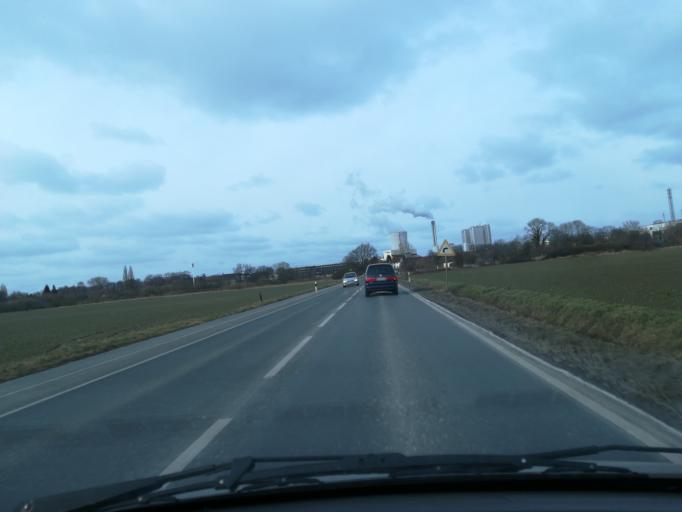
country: DE
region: Lower Saxony
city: Auf der Horst
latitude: 52.4098
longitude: 9.6463
